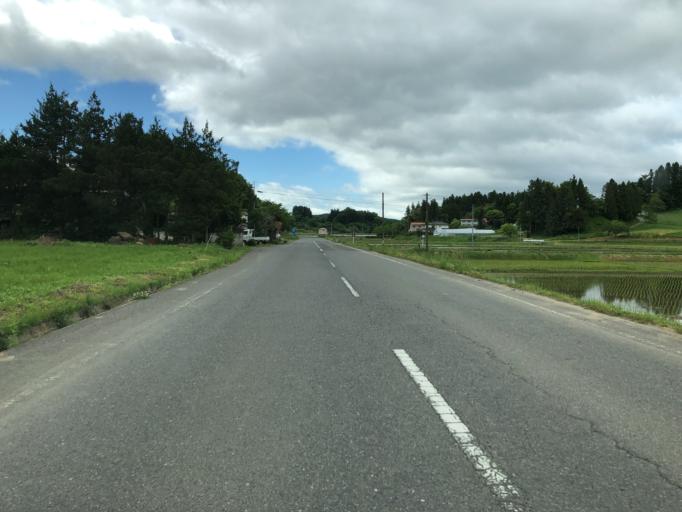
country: JP
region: Fukushima
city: Nihommatsu
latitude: 37.5224
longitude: 140.4736
